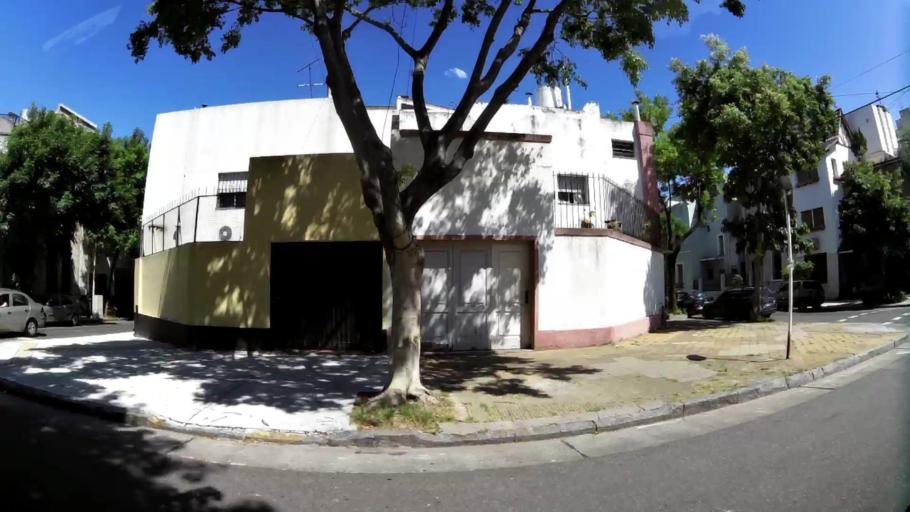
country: AR
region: Buenos Aires F.D.
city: Villa Santa Rita
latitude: -34.6328
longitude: -58.4388
